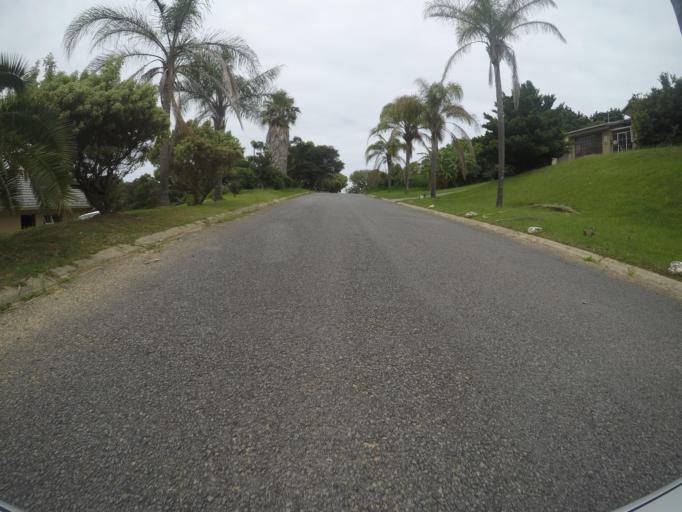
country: ZA
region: Eastern Cape
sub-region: Buffalo City Metropolitan Municipality
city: East London
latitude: -32.9756
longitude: 27.9501
